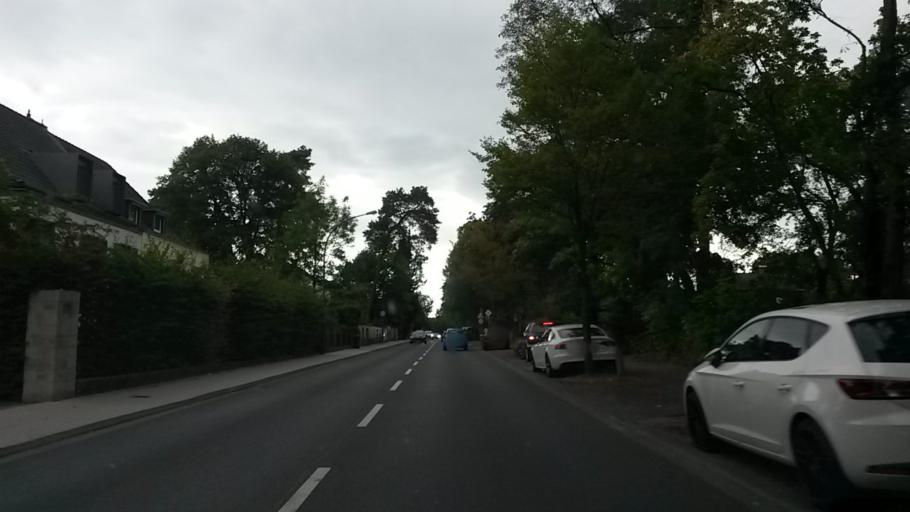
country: DE
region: North Rhine-Westphalia
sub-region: Regierungsbezirk Koln
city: Rath
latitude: 50.9208
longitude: 7.0978
